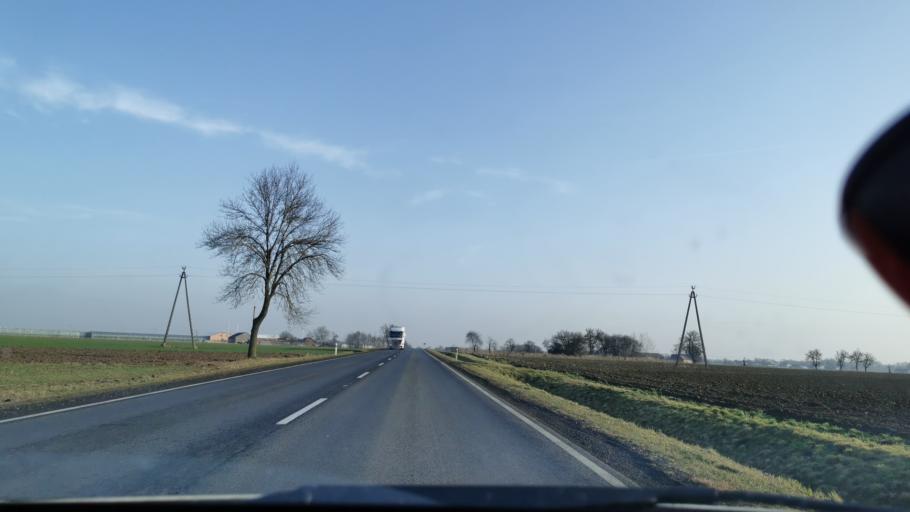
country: PL
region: Lodz Voivodeship
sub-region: Powiat sieradzki
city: Blaszki
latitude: 51.6819
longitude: 18.3390
